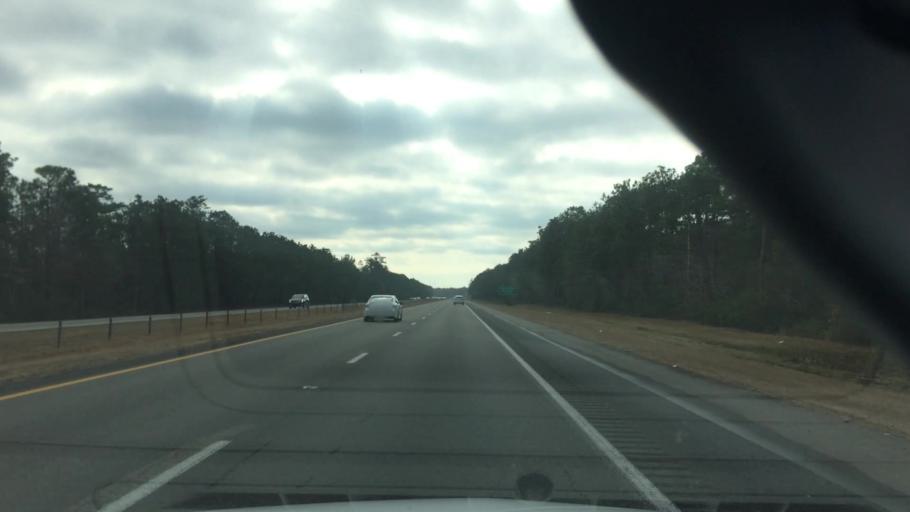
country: US
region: North Carolina
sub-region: New Hanover County
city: Castle Hayne
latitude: 34.3852
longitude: -77.8786
